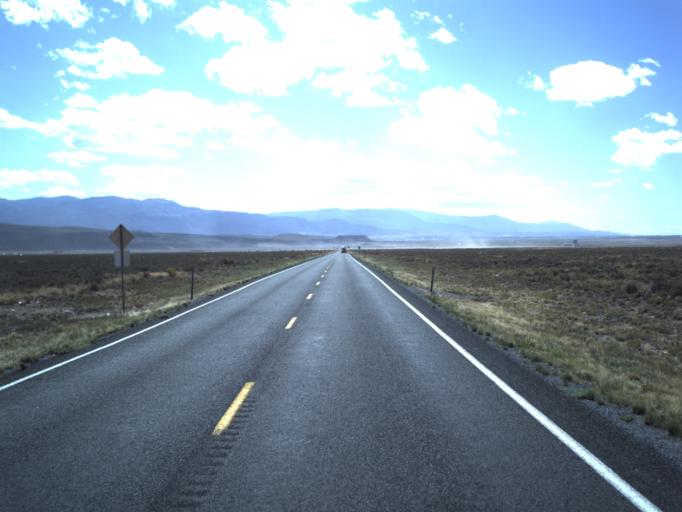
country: US
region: Utah
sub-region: Iron County
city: Enoch
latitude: 37.9232
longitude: -113.0315
